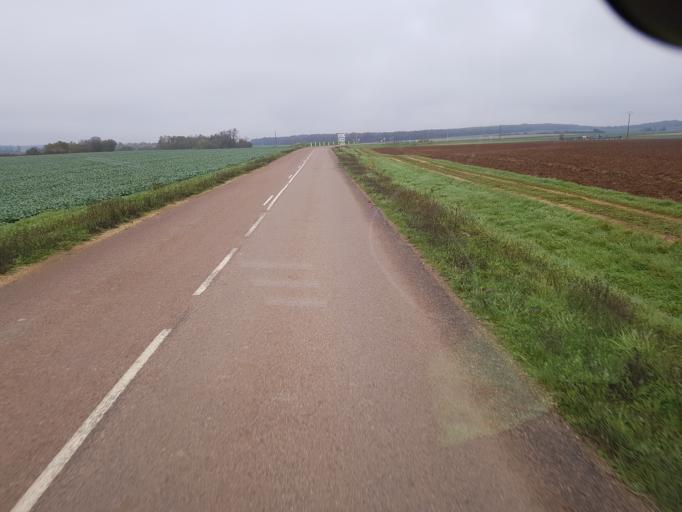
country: FR
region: Bourgogne
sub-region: Departement de la Cote-d'Or
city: Saint-Julien
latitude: 47.4278
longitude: 5.2097
